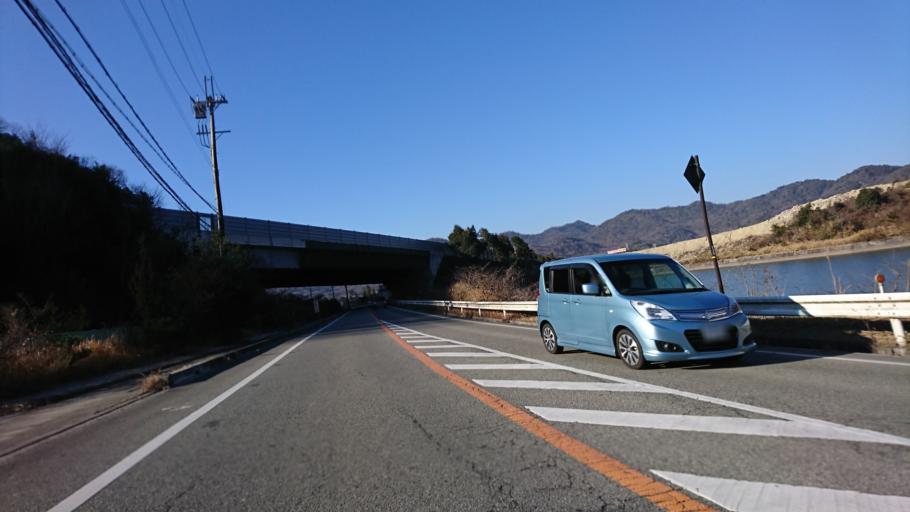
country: JP
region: Hyogo
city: Kakogawacho-honmachi
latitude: 34.8518
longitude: 134.8406
